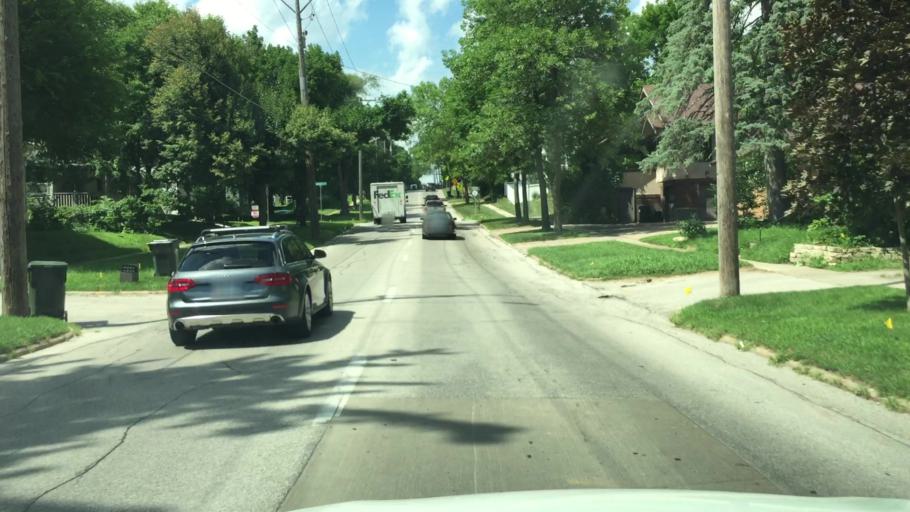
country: US
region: Iowa
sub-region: Johnson County
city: Iowa City
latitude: 41.6662
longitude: -91.5228
